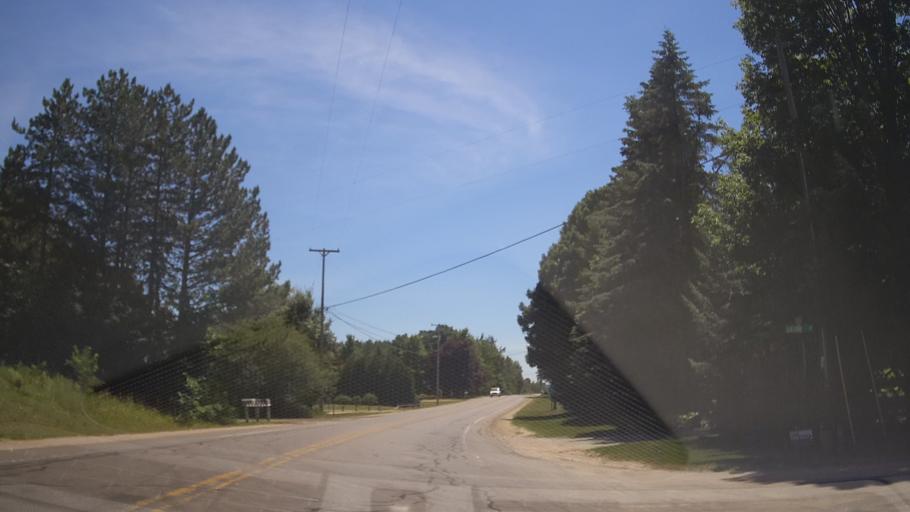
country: US
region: Michigan
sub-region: Grand Traverse County
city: Traverse City
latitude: 44.6871
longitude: -85.6896
